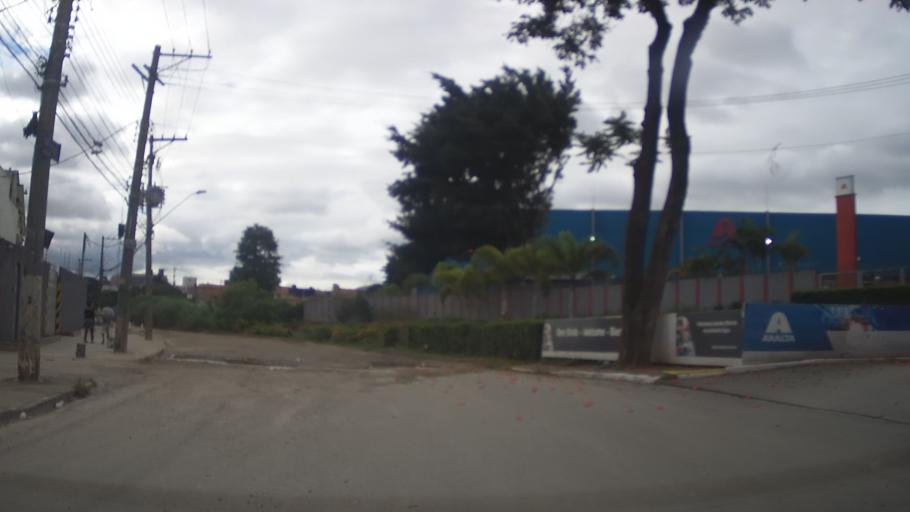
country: BR
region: Sao Paulo
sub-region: Guarulhos
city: Guarulhos
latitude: -23.4651
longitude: -46.4643
